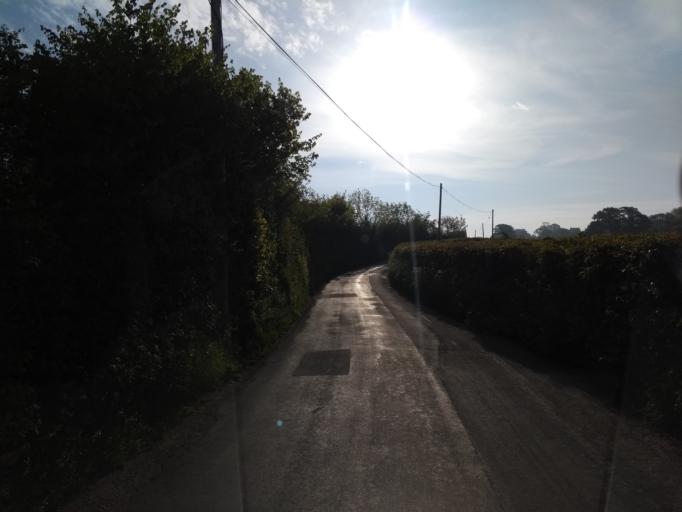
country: GB
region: England
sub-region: Devon
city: Axminster
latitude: 50.8053
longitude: -2.9450
